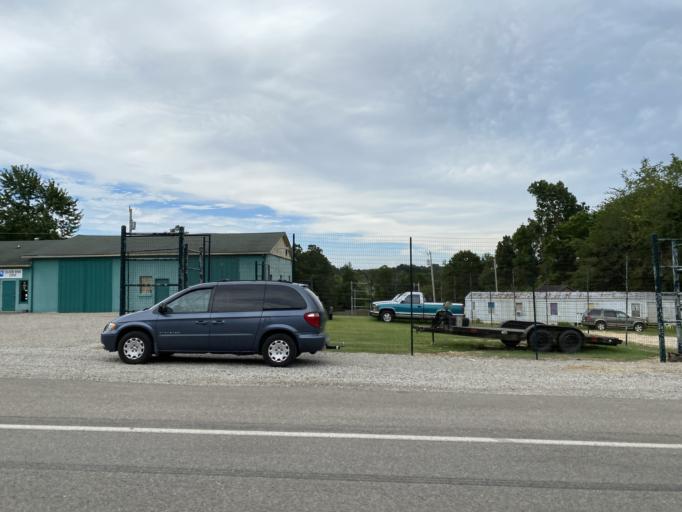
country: US
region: Arkansas
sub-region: Fulton County
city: Salem
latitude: 36.3646
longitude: -91.8284
